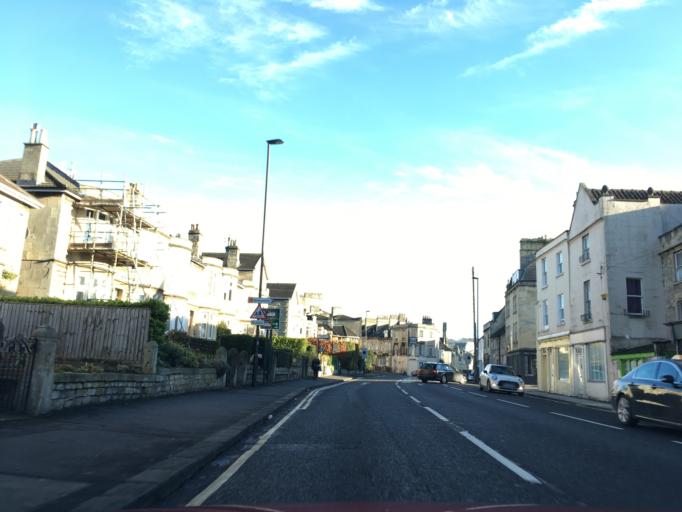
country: GB
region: England
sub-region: Bath and North East Somerset
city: Bath
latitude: 51.3836
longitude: -2.3688
